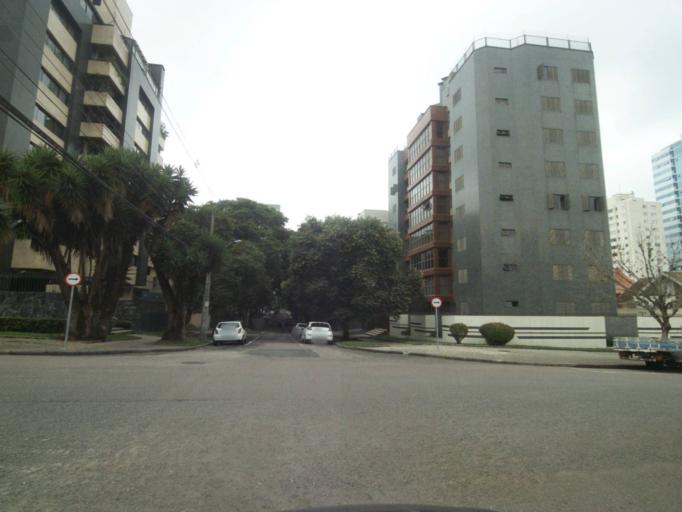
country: BR
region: Parana
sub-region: Curitiba
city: Curitiba
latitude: -25.4118
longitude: -49.2599
